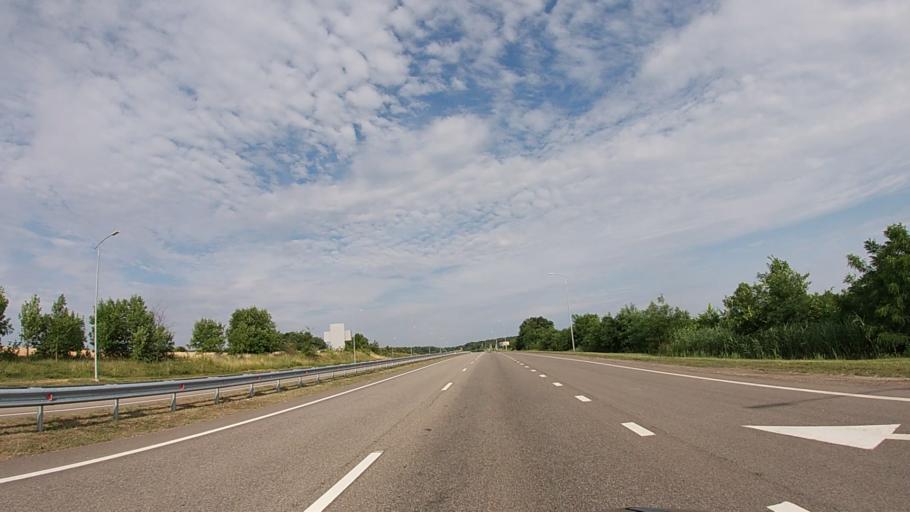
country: RU
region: Belgorod
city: Tomarovka
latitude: 50.6607
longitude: 36.3512
